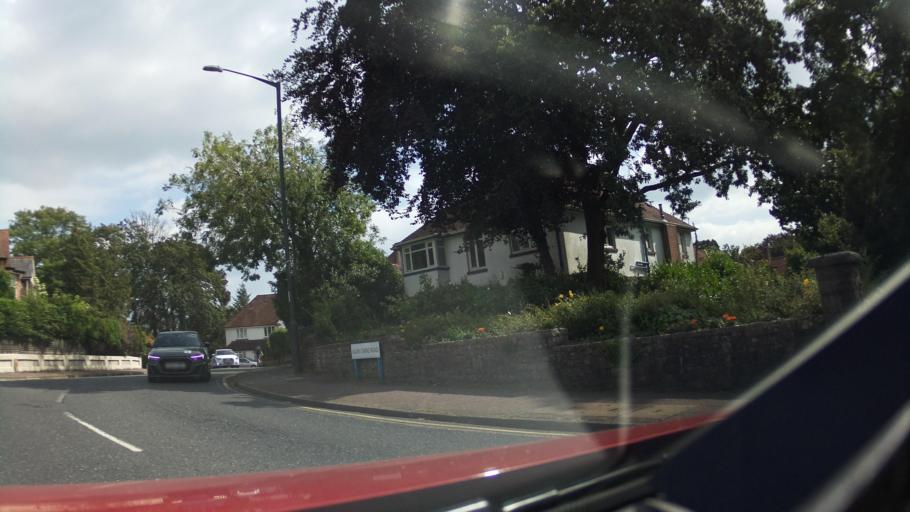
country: GB
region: England
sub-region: Bournemouth
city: Bournemouth
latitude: 50.7196
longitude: -1.9041
